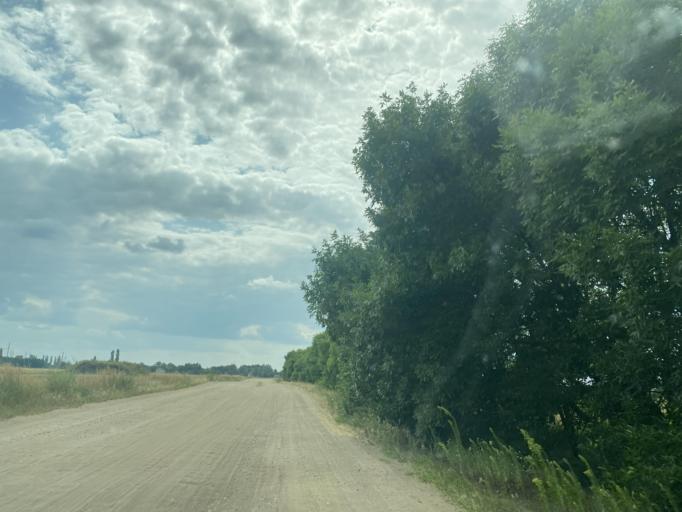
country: BY
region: Brest
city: Ivanava
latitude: 52.3588
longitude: 25.6332
